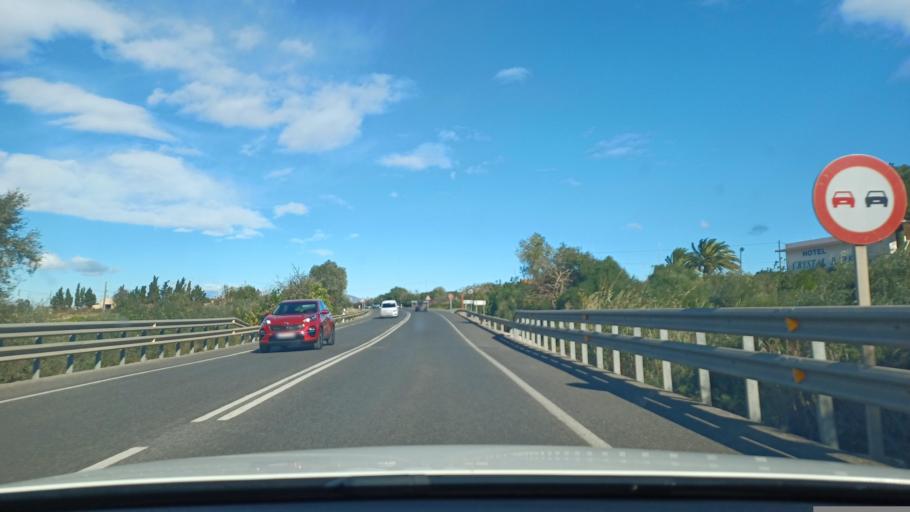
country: ES
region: Valencia
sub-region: Provincia de Castello
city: Vinaros
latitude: 40.4470
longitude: 0.4485
